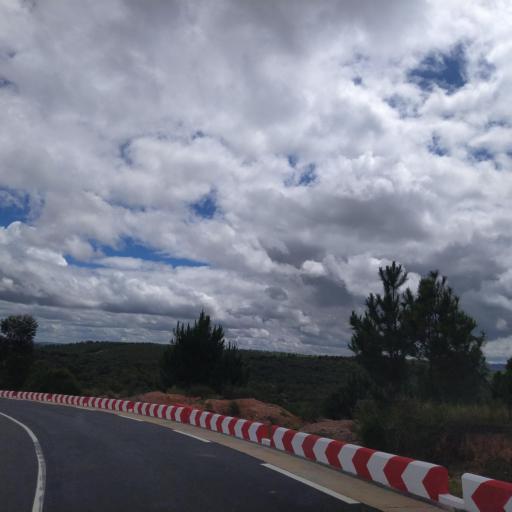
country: MG
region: Analamanga
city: Anjozorobe
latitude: -18.4805
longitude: 48.2645
